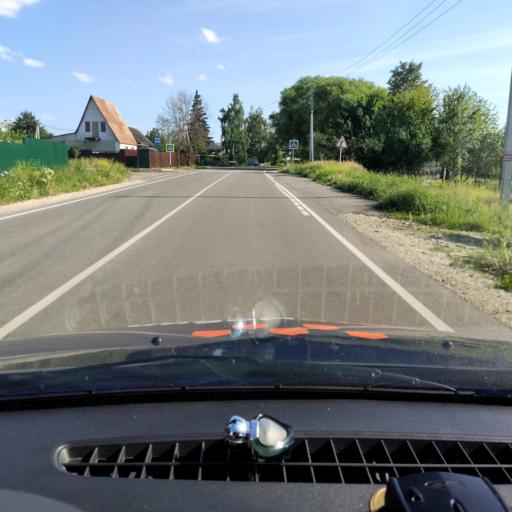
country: RU
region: Voronezj
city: Devitsa
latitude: 51.6509
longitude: 38.9727
